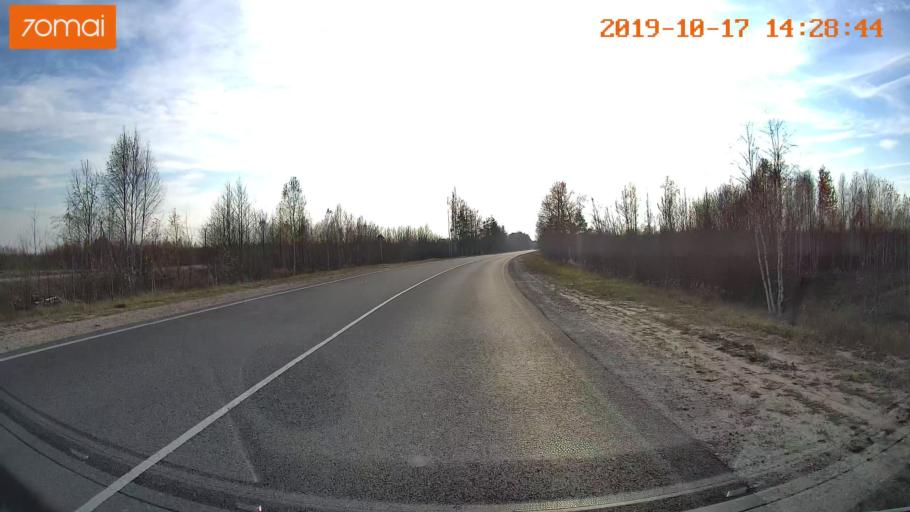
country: RU
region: Rjazan
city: Solotcha
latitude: 54.9693
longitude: 39.9509
